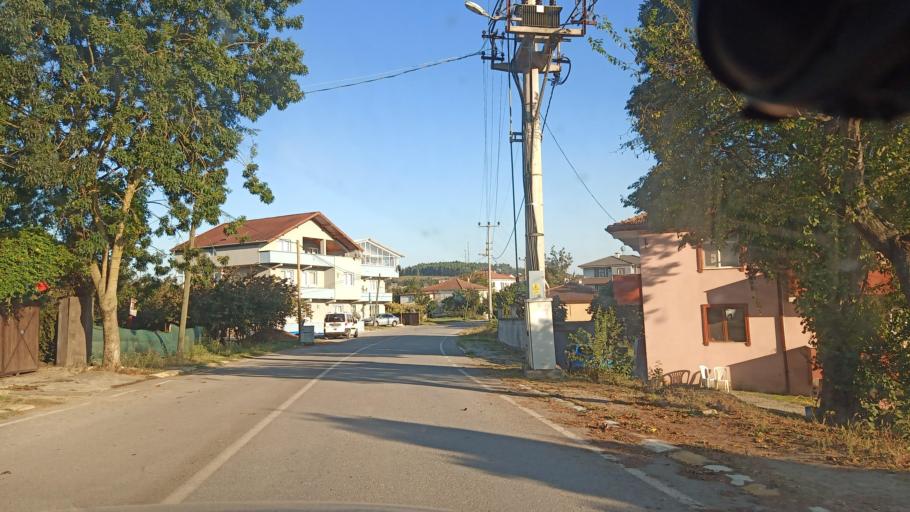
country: TR
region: Sakarya
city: Ferizli
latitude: 40.9460
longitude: 30.4836
